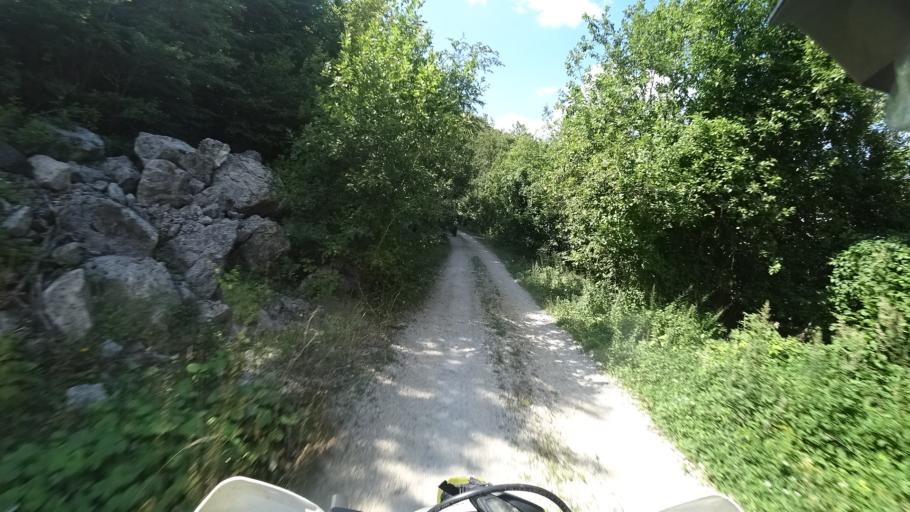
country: HR
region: Zadarska
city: Gracac
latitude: 44.4497
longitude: 15.9827
